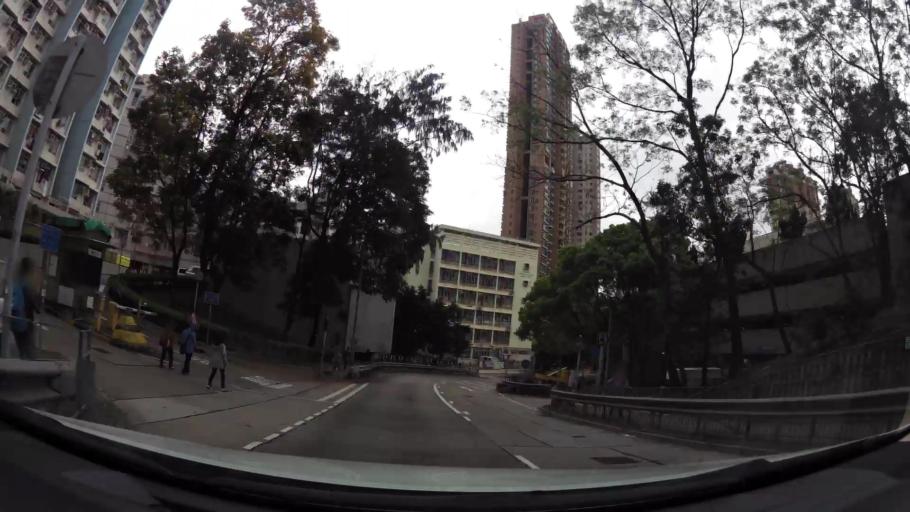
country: HK
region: Wong Tai Sin
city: Wong Tai Sin
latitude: 22.3470
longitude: 114.1996
